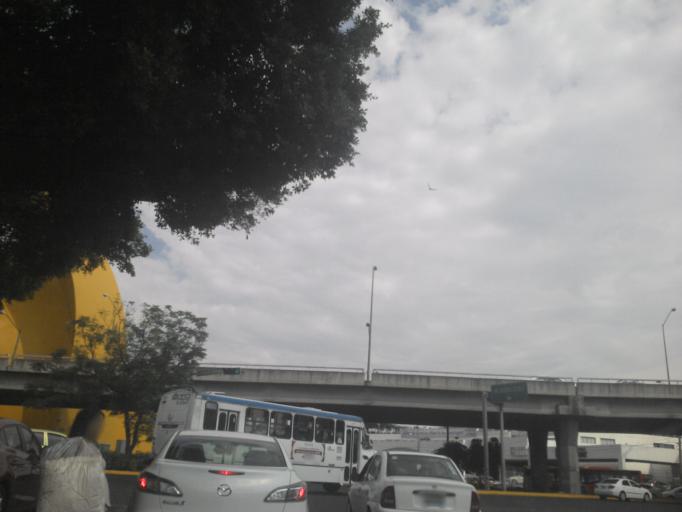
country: MX
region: Jalisco
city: Guadalajara
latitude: 20.6596
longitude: -103.3847
